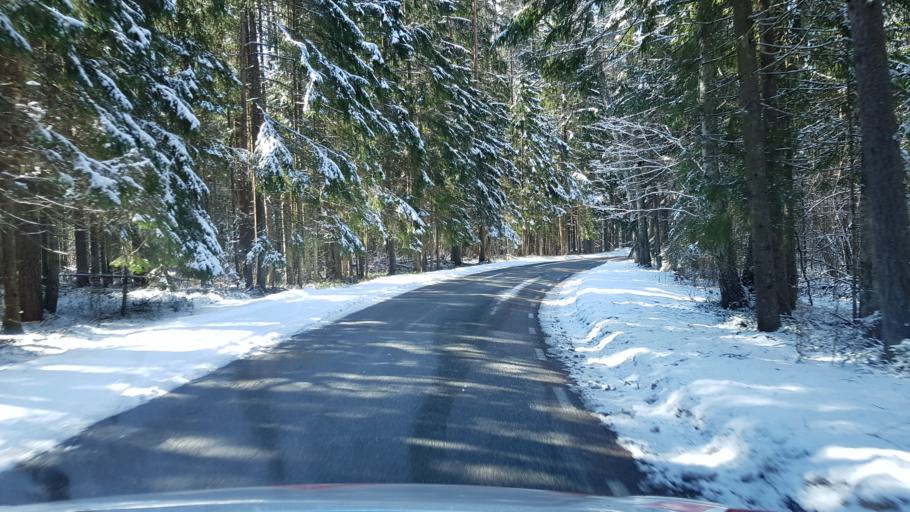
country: EE
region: Laeaene-Virumaa
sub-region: Kadrina vald
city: Kadrina
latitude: 59.5182
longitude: 25.9858
